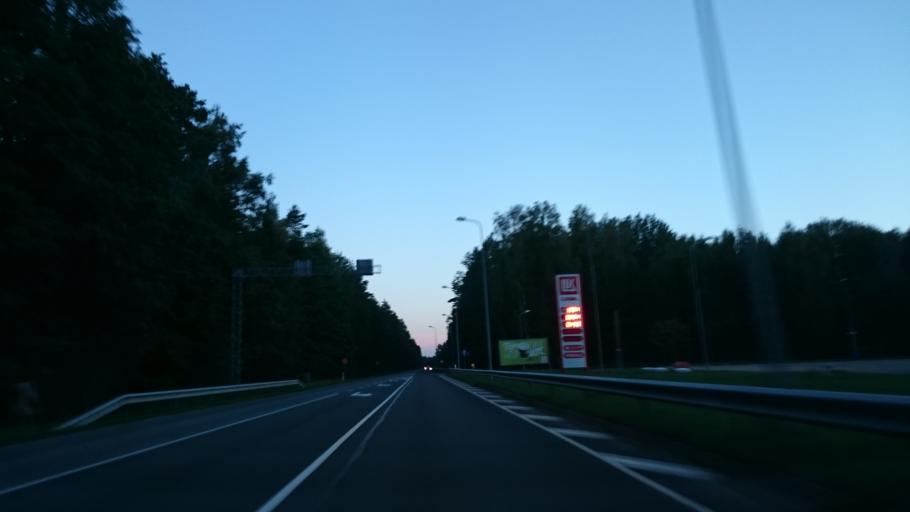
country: LV
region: Saulkrastu
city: Saulkrasti
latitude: 57.2255
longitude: 24.3915
